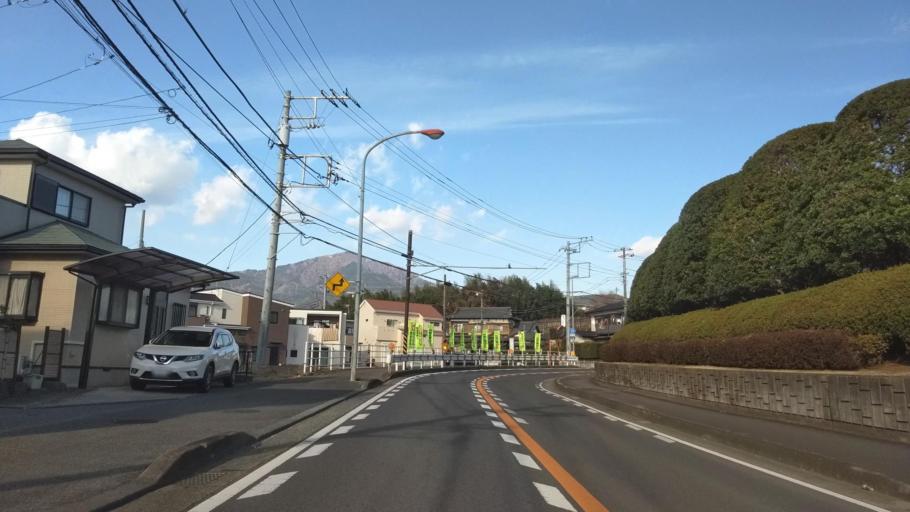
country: JP
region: Kanagawa
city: Hadano
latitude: 35.3812
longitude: 139.2363
